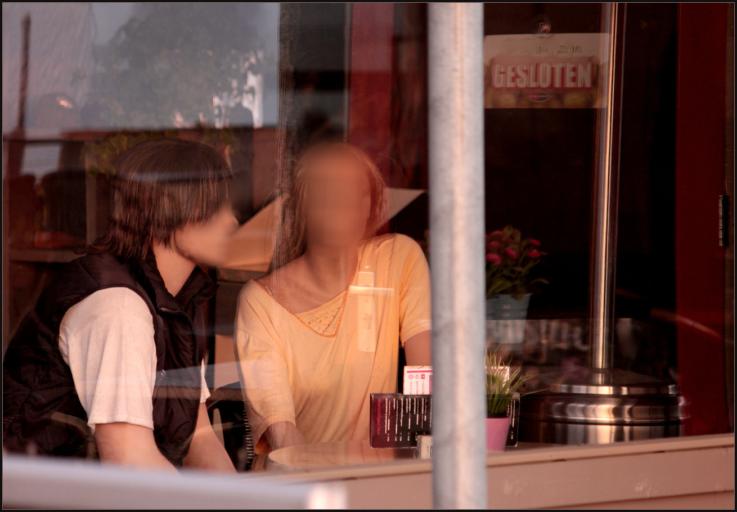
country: DE
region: North Rhine-Westphalia
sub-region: Regierungsbezirk Dusseldorf
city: Emmerich
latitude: 51.8294
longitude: 6.2464
